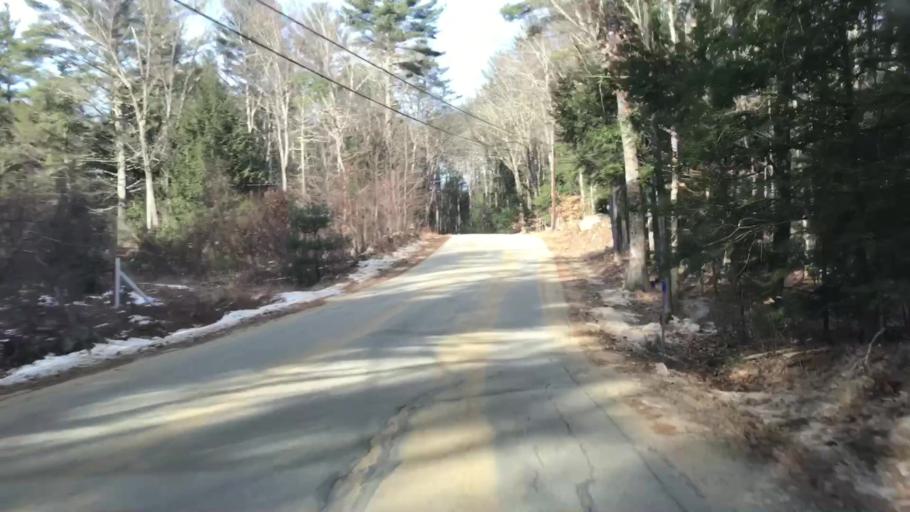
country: US
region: New Hampshire
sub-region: Hillsborough County
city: Mont Vernon
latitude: 42.9093
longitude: -71.6068
